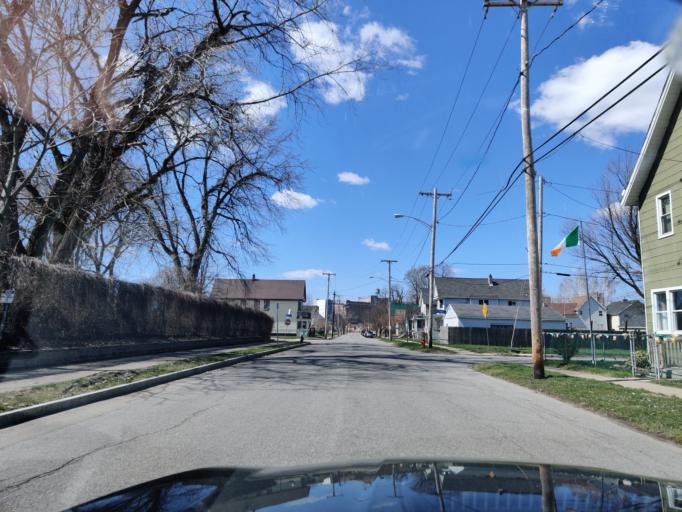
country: US
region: New York
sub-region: Erie County
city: Buffalo
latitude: 42.8646
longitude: -78.8634
